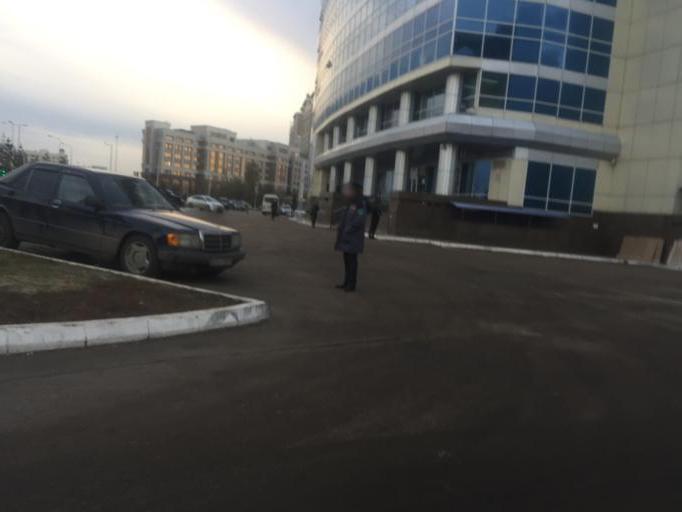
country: KZ
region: Astana Qalasy
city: Astana
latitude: 51.1345
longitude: 71.4142
